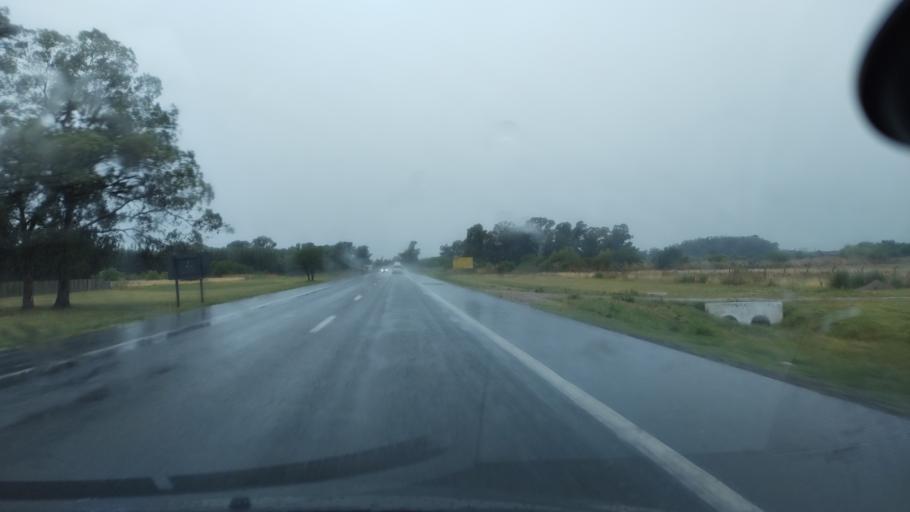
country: AR
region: Buenos Aires
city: Canuelas
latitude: -35.0552
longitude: -58.7855
